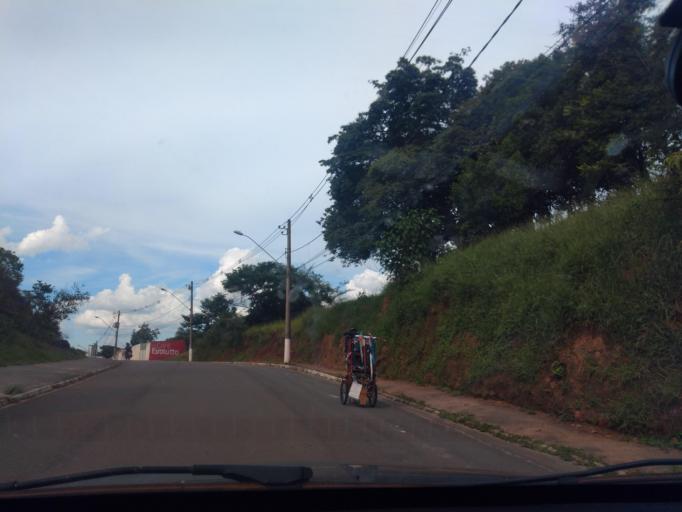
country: BR
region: Minas Gerais
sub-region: Tres Coracoes
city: Tres Coracoes
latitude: -21.7092
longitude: -45.2615
